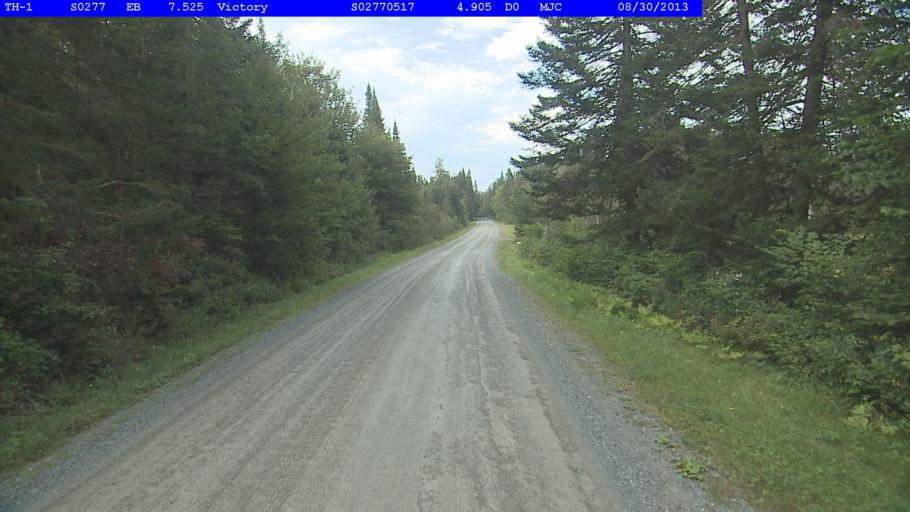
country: US
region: Vermont
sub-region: Caledonia County
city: Lyndonville
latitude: 44.5398
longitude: -71.7873
